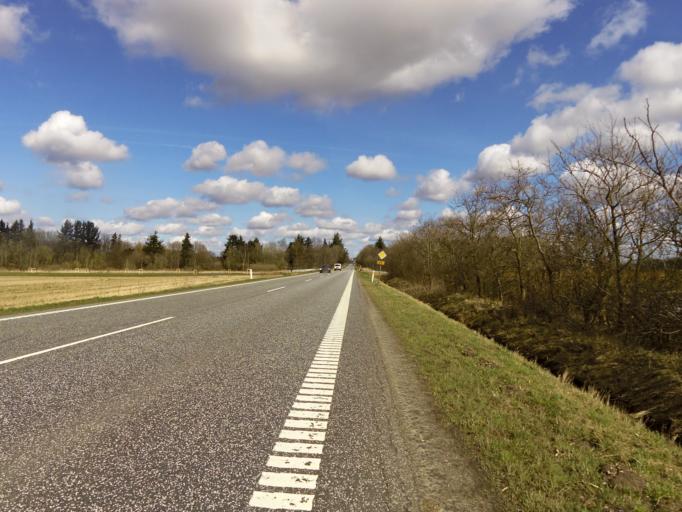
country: DK
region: South Denmark
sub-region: Tonder Kommune
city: Toftlund
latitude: 55.1707
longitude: 9.0532
